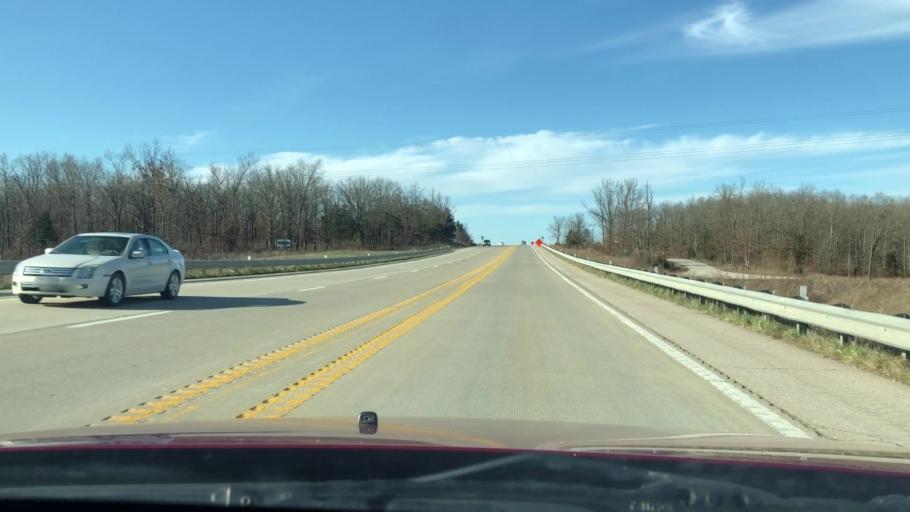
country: US
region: Missouri
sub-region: Camden County
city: Camdenton
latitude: 37.9443
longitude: -92.7157
